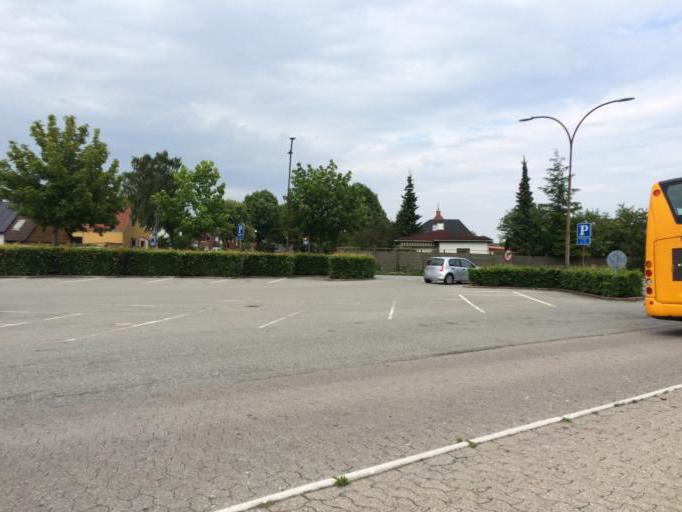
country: DK
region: Capital Region
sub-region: Rodovre Kommune
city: Rodovre
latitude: 55.6652
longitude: 12.4591
